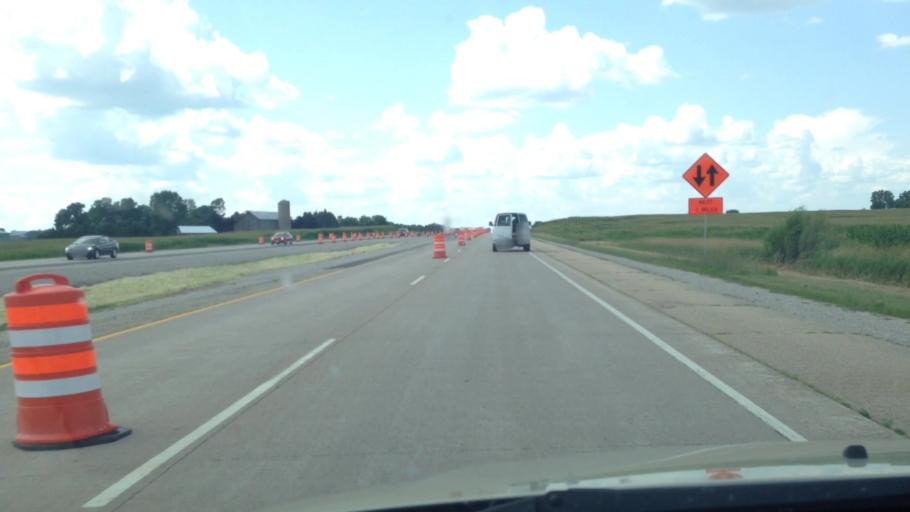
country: US
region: Wisconsin
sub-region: Brown County
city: Pulaski
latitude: 44.6901
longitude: -88.3271
